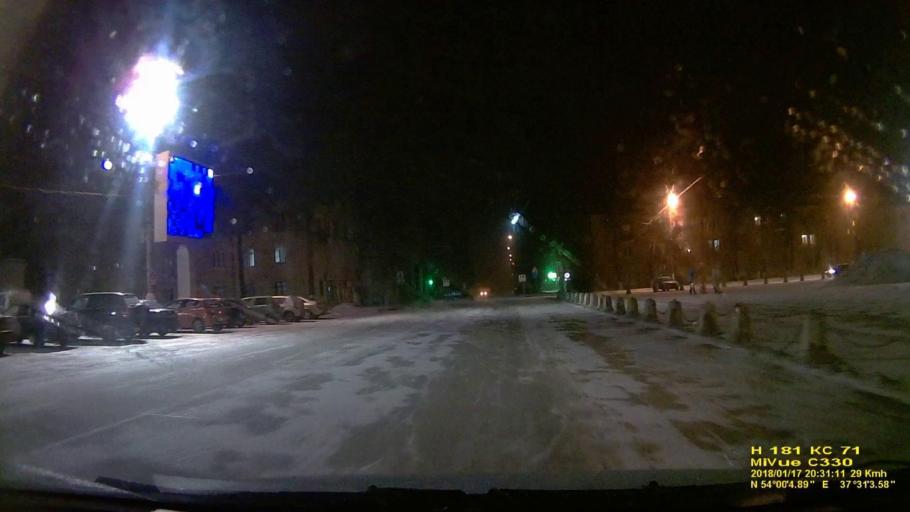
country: RU
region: Tula
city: Shchekino
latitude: 54.0015
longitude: 37.5177
